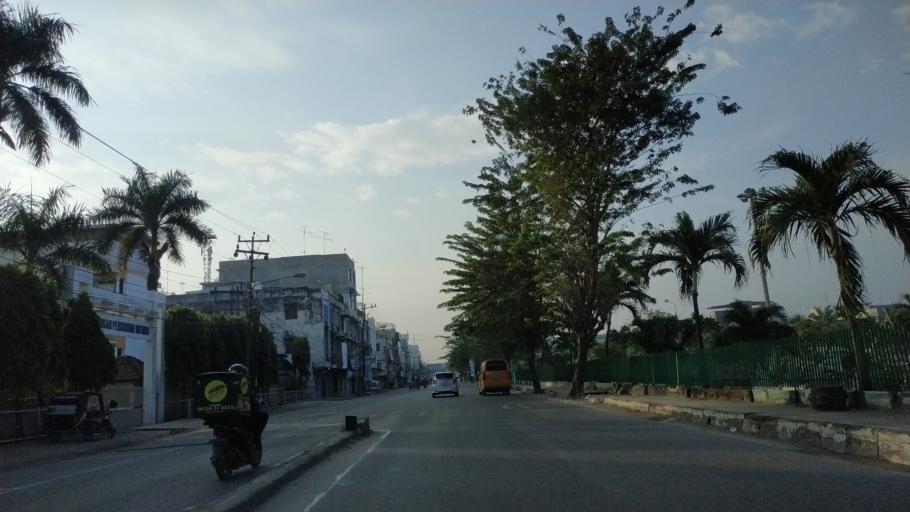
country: ID
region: North Sumatra
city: Medan
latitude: 3.5920
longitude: 98.6893
